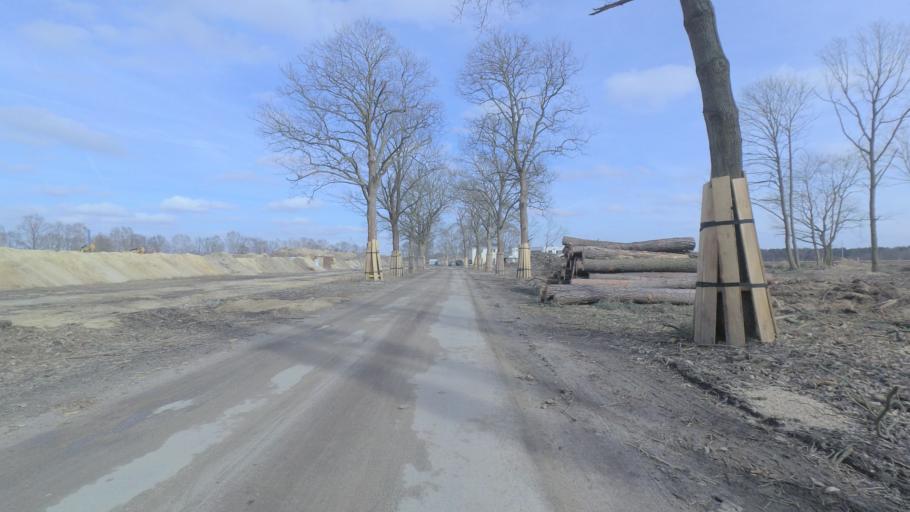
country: DE
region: Brandenburg
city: Ludwigsfelde
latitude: 52.3155
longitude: 13.2156
